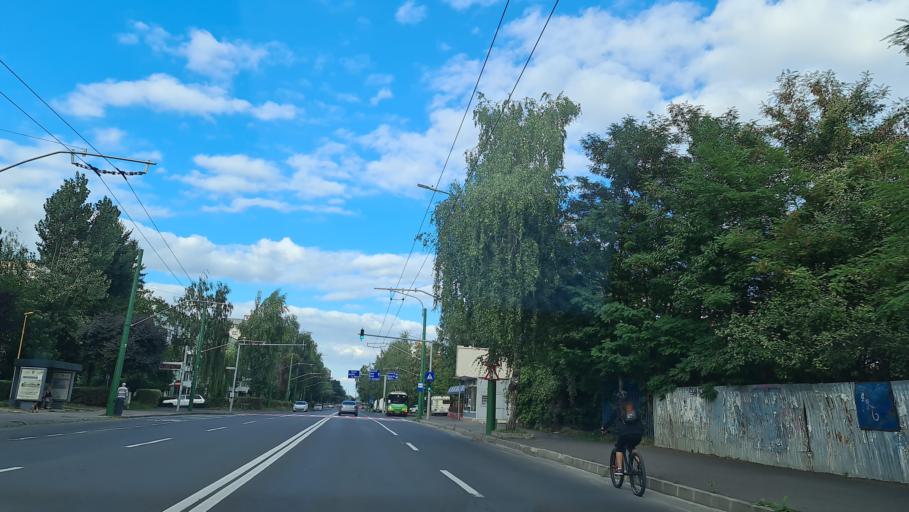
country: RO
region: Brasov
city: Brasov
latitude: 45.6560
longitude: 25.6180
